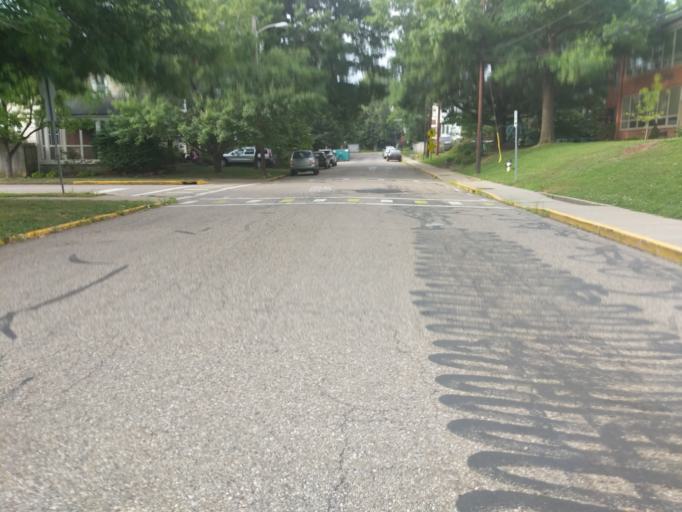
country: US
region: Ohio
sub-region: Athens County
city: Athens
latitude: 39.3346
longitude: -82.0943
